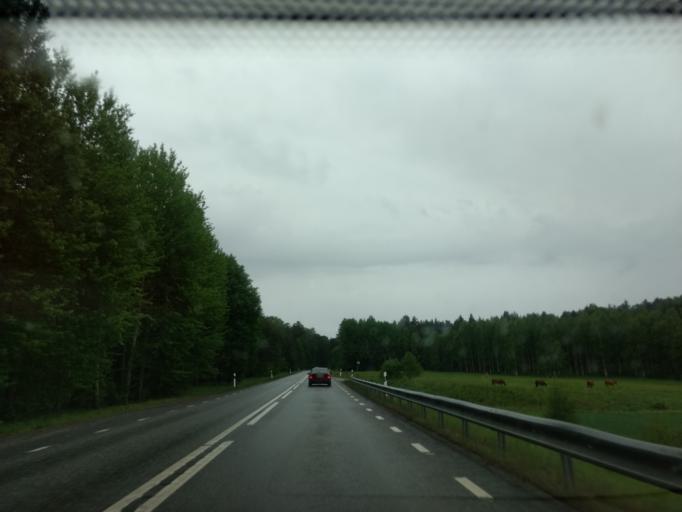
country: SE
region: Uppsala
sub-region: Uppsala Kommun
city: Saevja
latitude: 59.7806
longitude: 17.6638
